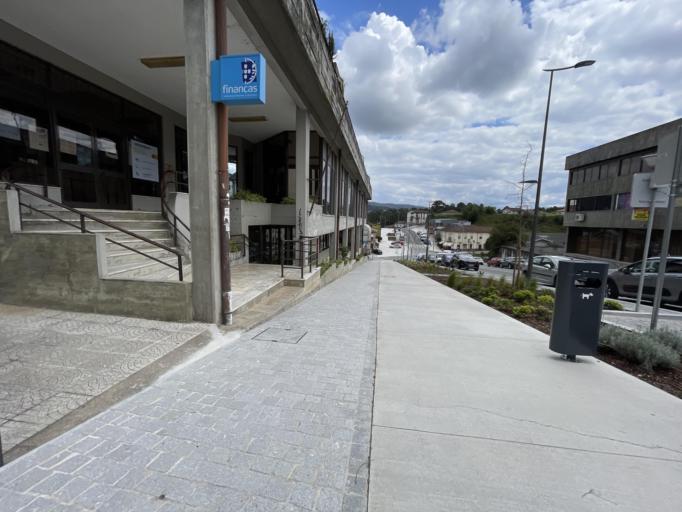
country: PT
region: Porto
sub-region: Marco de Canaveses
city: Marco de Canavezes
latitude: 41.1839
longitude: -8.1463
